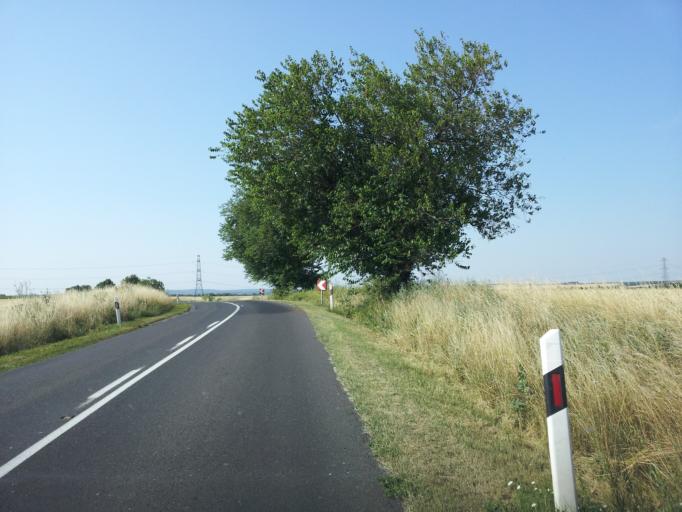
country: HU
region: Fejer
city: Lovasbereny
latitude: 47.4006
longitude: 18.5854
